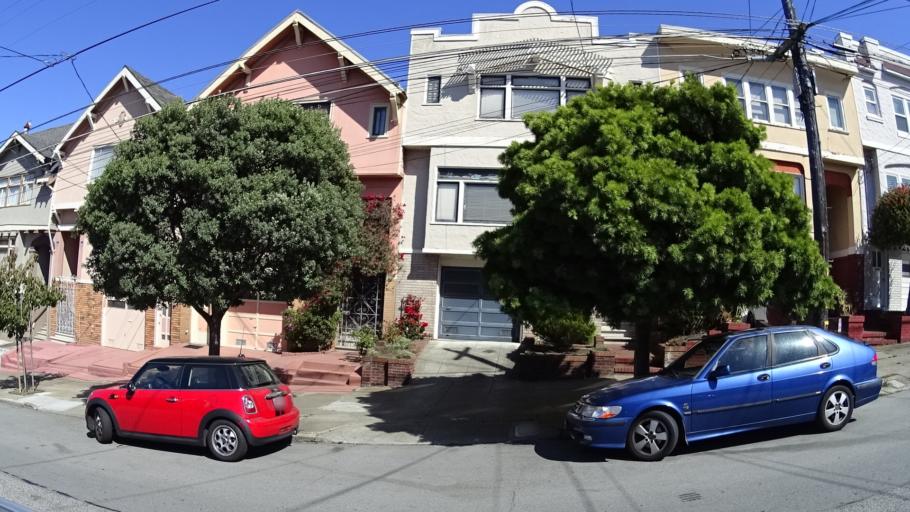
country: US
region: California
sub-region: San Francisco County
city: San Francisco
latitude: 37.7606
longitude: -122.4704
